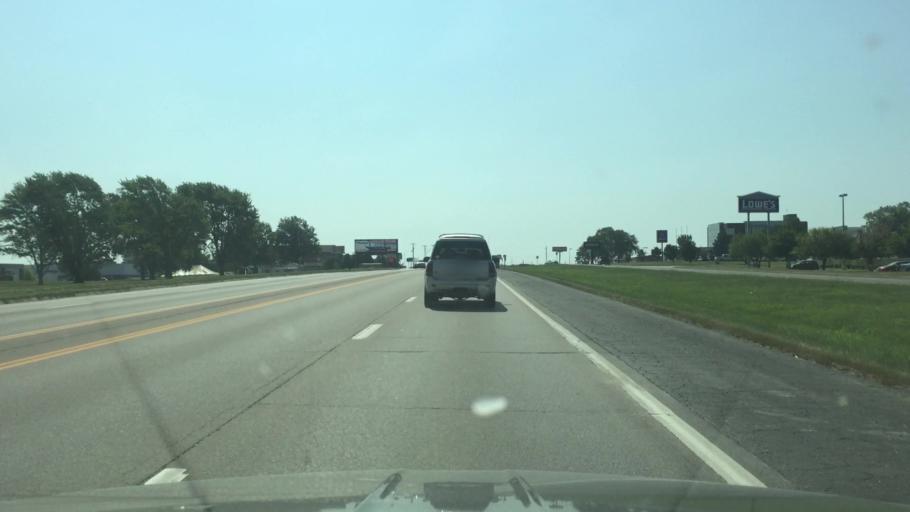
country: US
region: Missouri
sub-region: Pettis County
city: Sedalia
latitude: 38.7126
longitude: -93.2769
